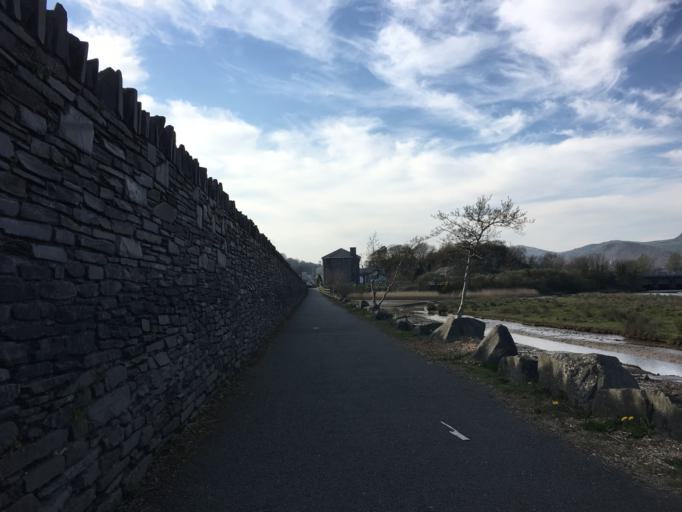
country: GB
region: Wales
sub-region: Gwynedd
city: Porthmadog
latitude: 52.9234
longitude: -4.1224
